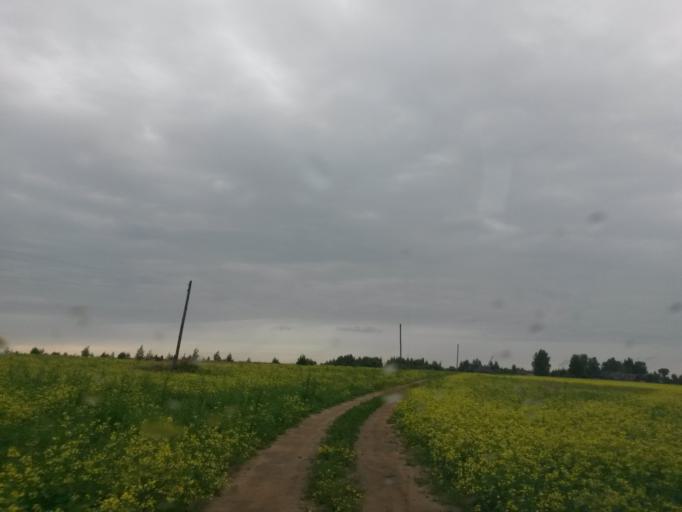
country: RU
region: Jaroslavl
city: Tutayev
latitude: 57.9415
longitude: 39.4408
